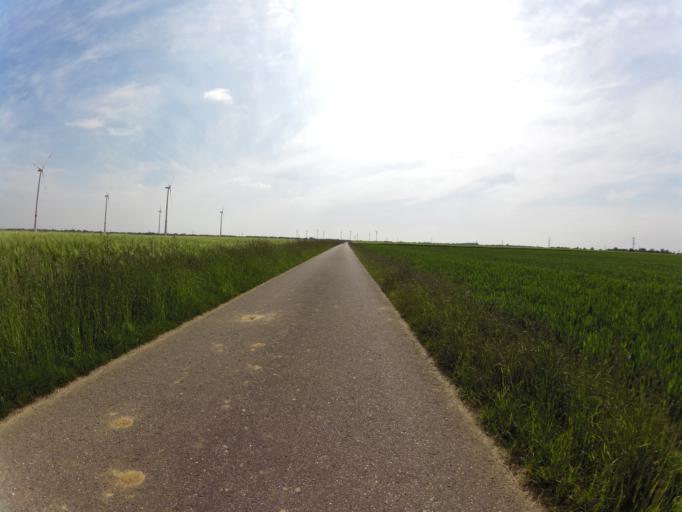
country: DE
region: North Rhine-Westphalia
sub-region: Regierungsbezirk Koln
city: Aldenhoven
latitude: 50.8867
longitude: 6.2945
